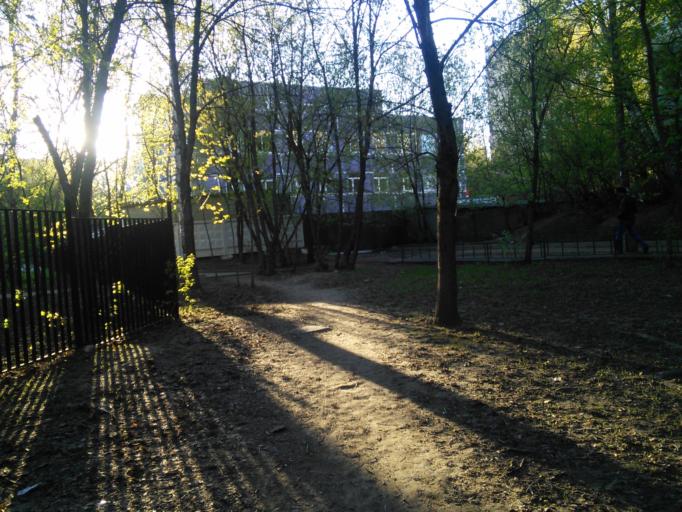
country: RU
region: Moscow
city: Troparevo
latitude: 55.6578
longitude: 37.4880
